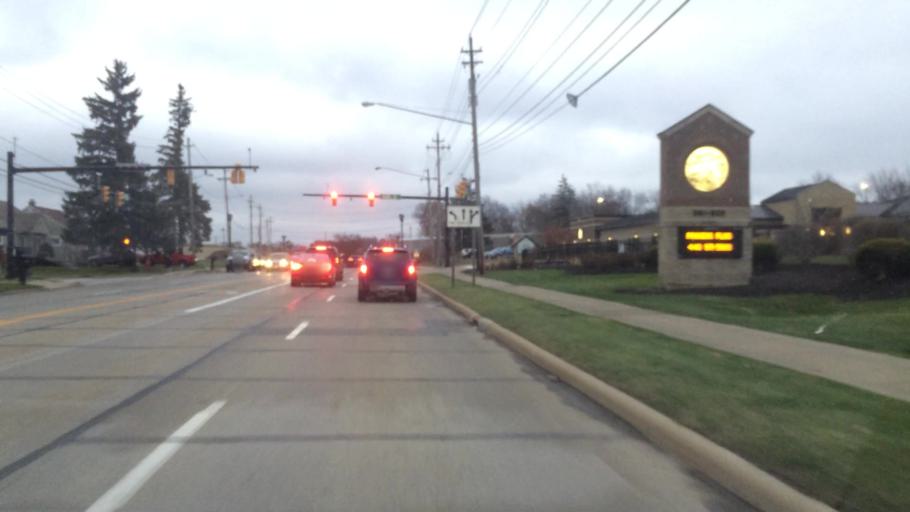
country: US
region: Ohio
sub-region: Cuyahoga County
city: Berea
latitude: 41.3723
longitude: -81.8755
